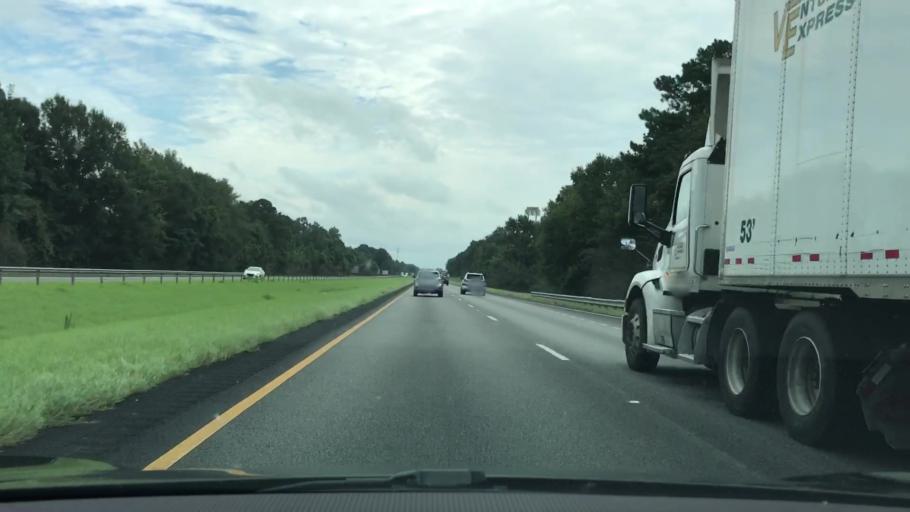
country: US
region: Alabama
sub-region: Elmore County
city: Tallassee
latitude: 32.4103
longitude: -85.9534
